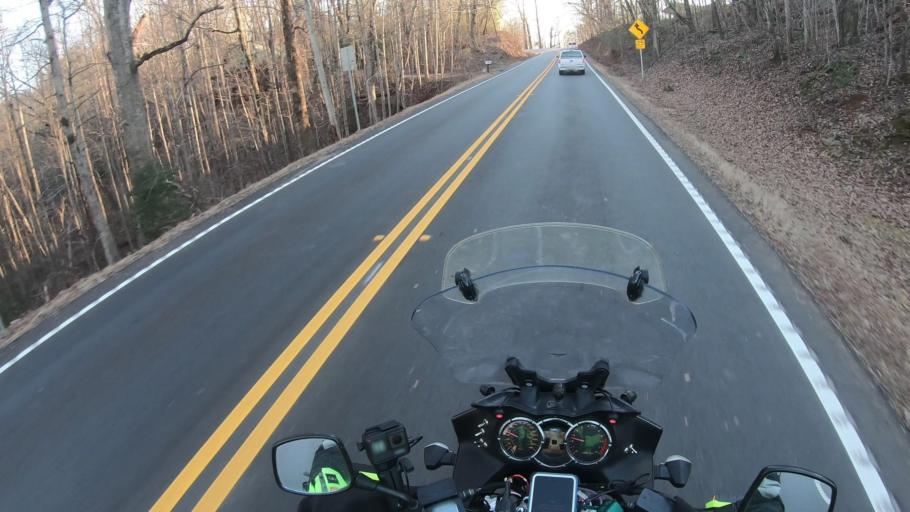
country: US
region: Georgia
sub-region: Lumpkin County
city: Dahlonega
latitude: 34.5880
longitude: -83.9698
